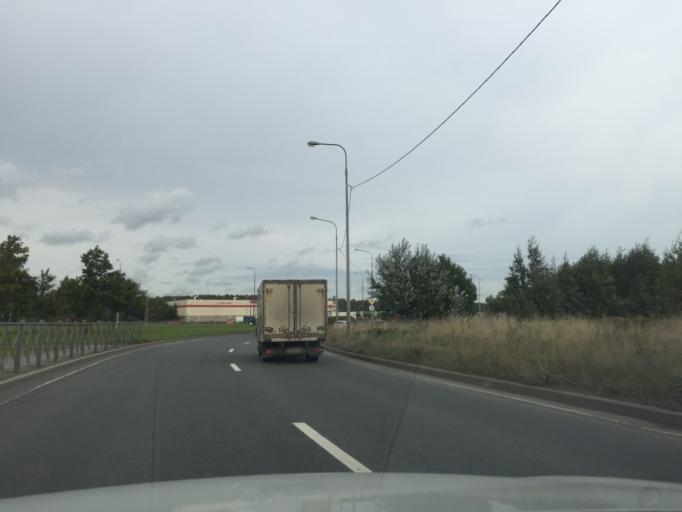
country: RU
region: St.-Petersburg
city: Krasnogvargeisky
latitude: 59.9869
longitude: 30.4614
